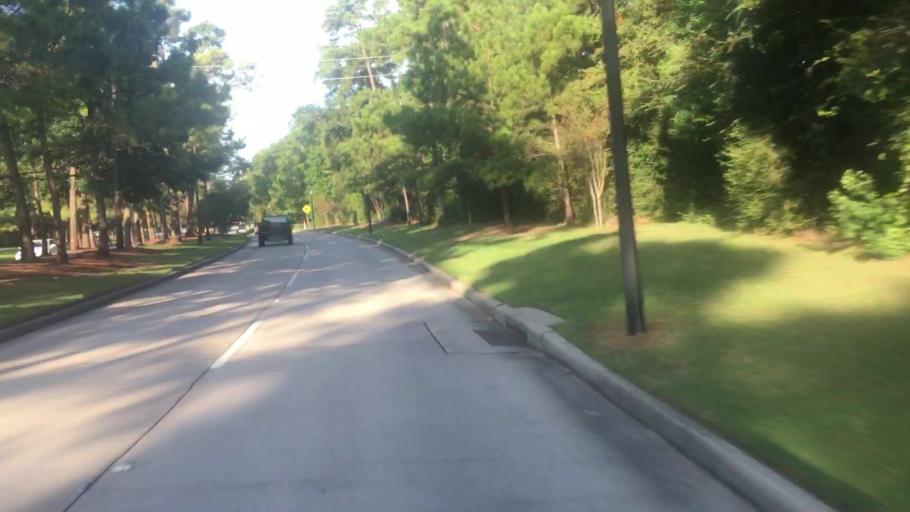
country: US
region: Texas
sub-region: Harris County
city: Atascocita
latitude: 29.9805
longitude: -95.1806
